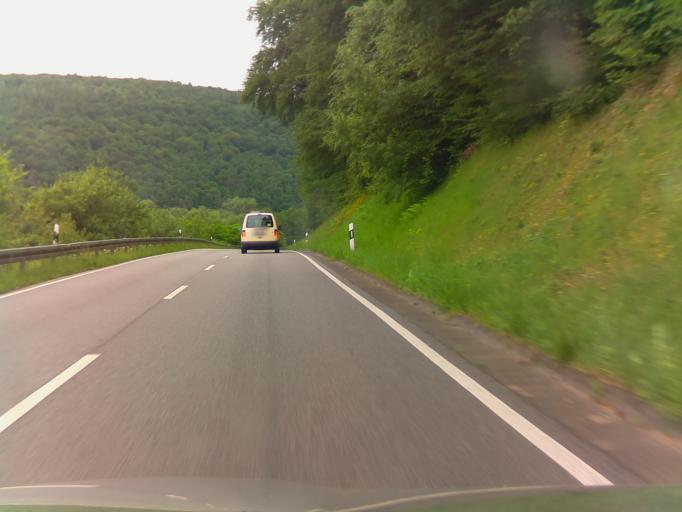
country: DE
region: Bavaria
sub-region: Regierungsbezirk Unterfranken
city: Schonau
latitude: 50.0970
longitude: 9.7308
